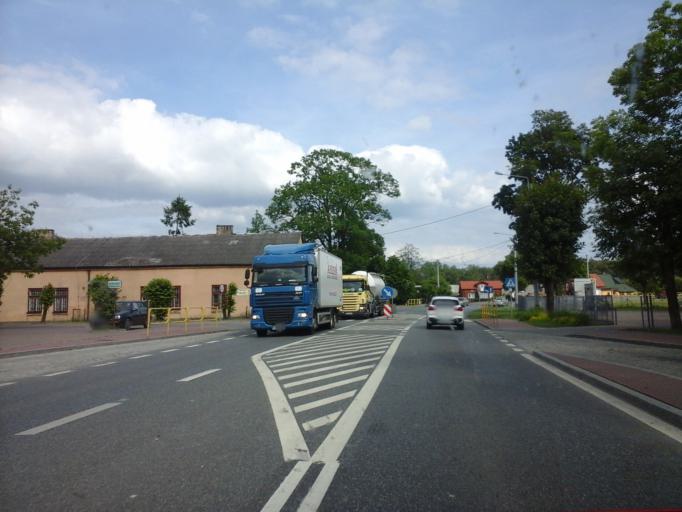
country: PL
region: Lodz Voivodeship
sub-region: Powiat opoczynski
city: Paradyz
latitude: 51.3054
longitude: 20.1153
